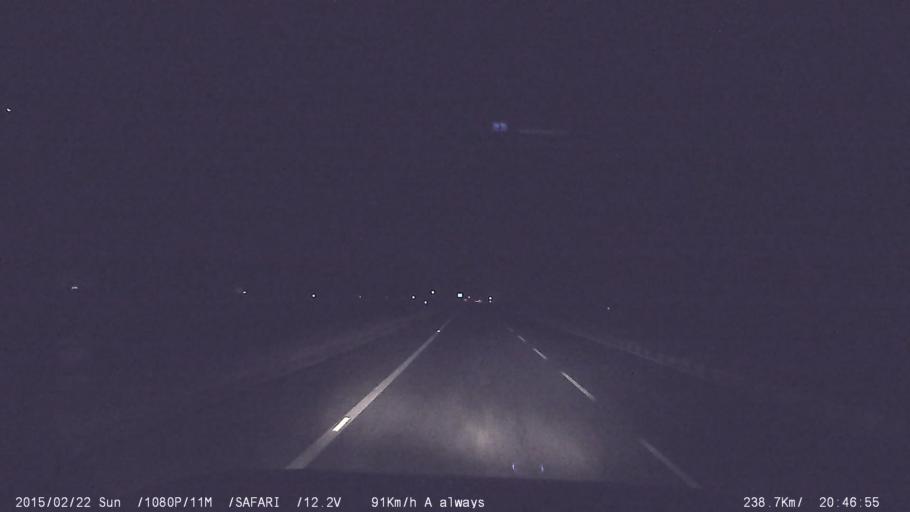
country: IN
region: Tamil Nadu
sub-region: Dindigul
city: Vedasandur
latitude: 10.4882
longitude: 77.9473
